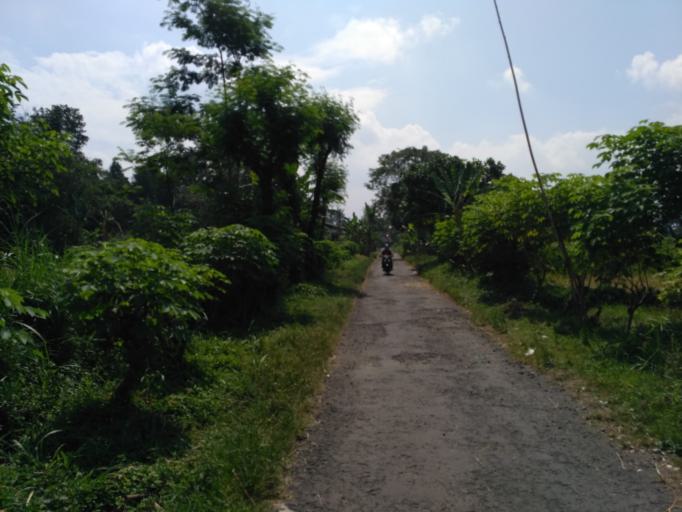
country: ID
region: Daerah Istimewa Yogyakarta
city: Depok
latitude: -7.7183
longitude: 110.4185
